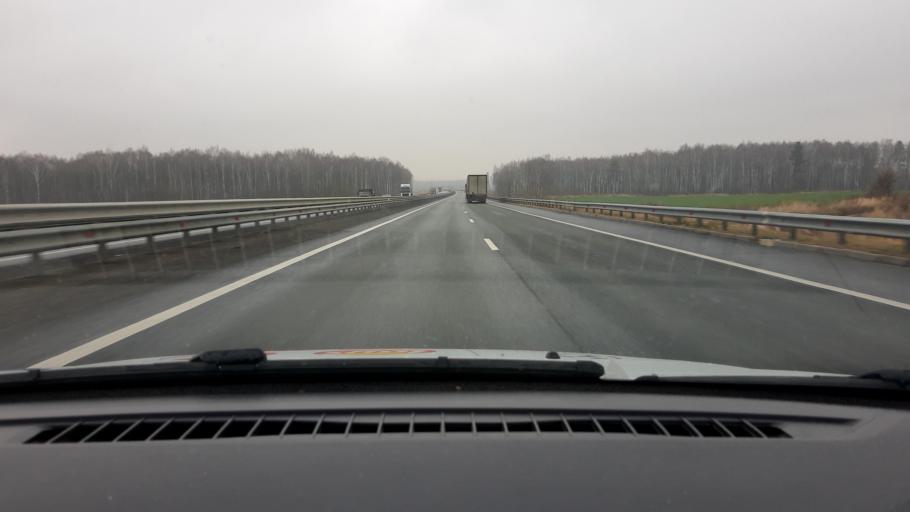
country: RU
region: Nizjnij Novgorod
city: Burevestnik
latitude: 56.1176
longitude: 43.8199
